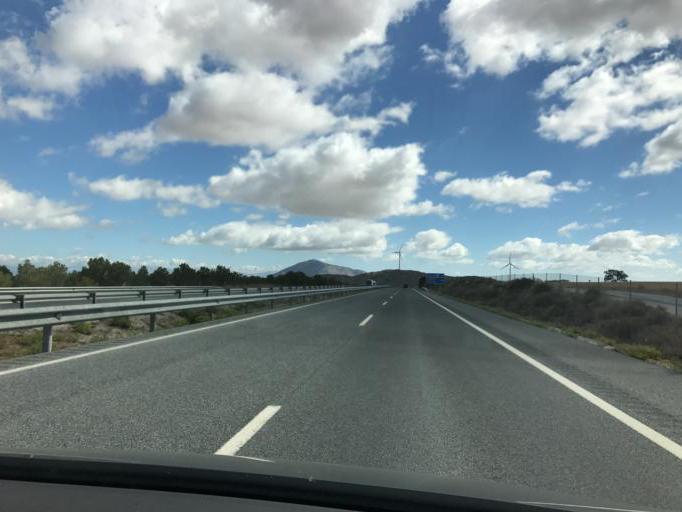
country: ES
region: Andalusia
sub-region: Provincia de Granada
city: Zujar
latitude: 37.4783
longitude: -2.8545
